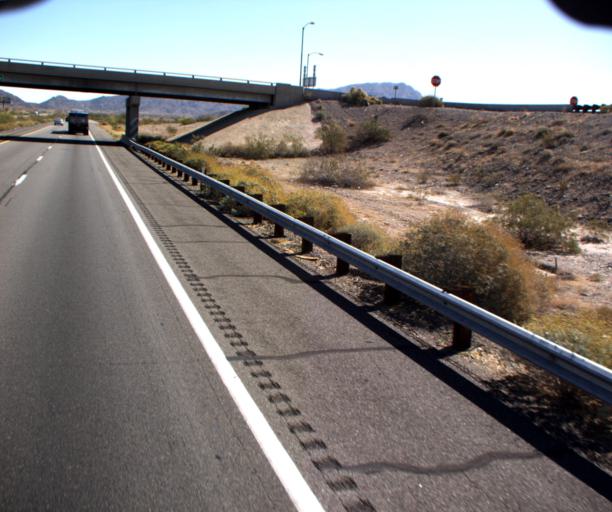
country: US
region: Arizona
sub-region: La Paz County
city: Ehrenberg
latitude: 33.6240
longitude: -114.4345
